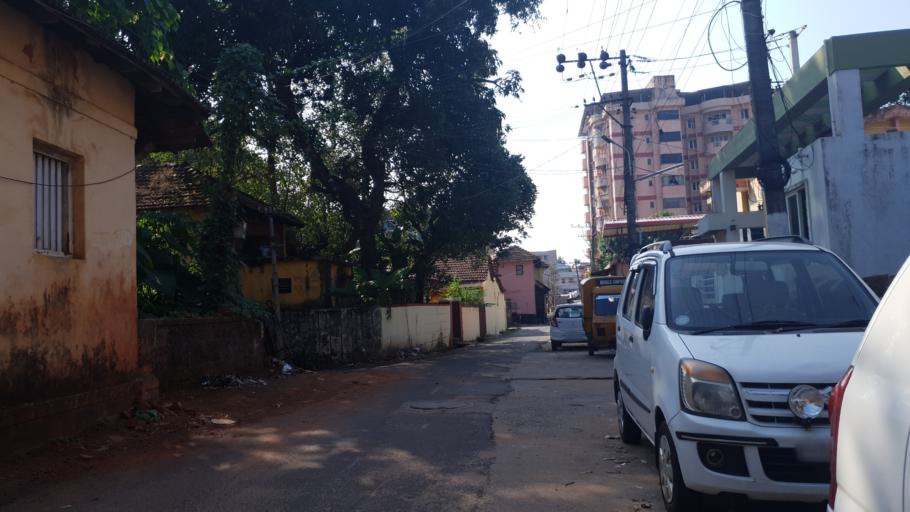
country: IN
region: Karnataka
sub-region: Dakshina Kannada
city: Mangalore
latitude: 12.8725
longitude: 74.8368
